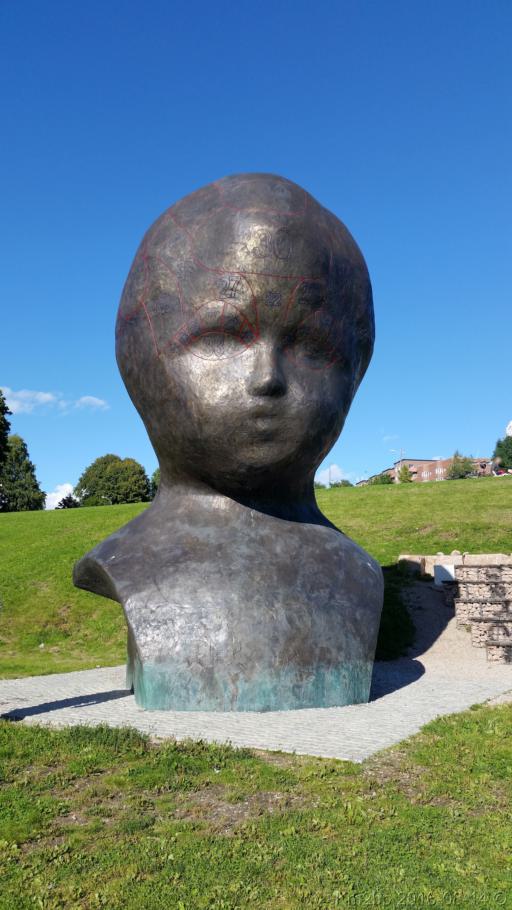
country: NO
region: Oslo
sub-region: Oslo
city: Oslo
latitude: 59.9339
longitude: 10.7767
